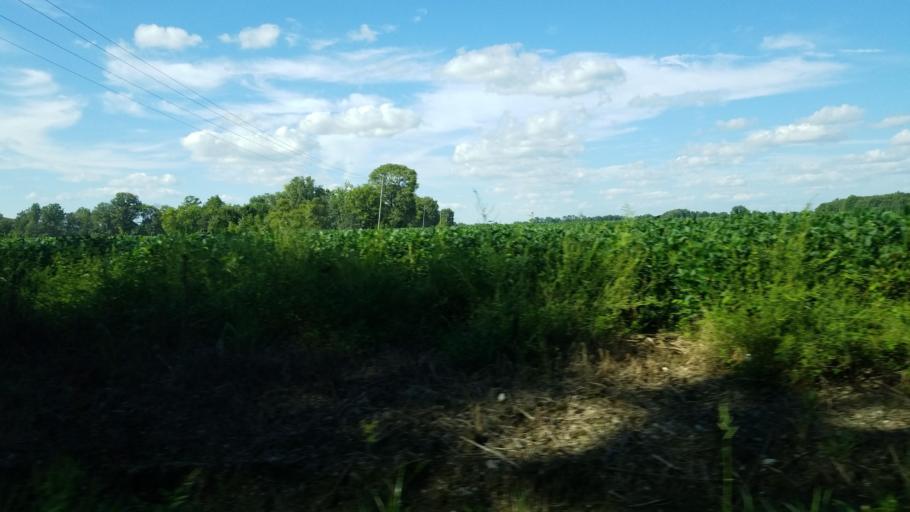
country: US
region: Illinois
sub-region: Saline County
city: Harrisburg
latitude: 37.8126
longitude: -88.5671
